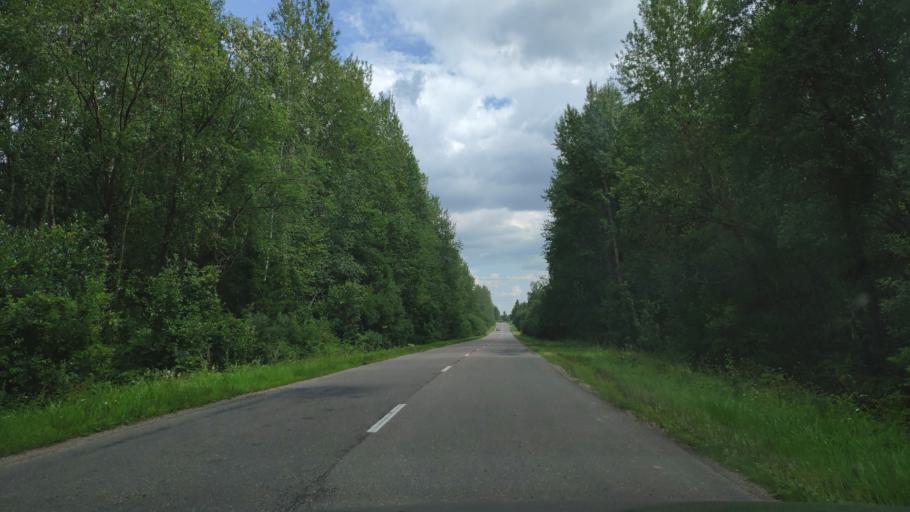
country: BY
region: Minsk
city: Khatsyezhyna
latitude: 53.8776
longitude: 27.2893
